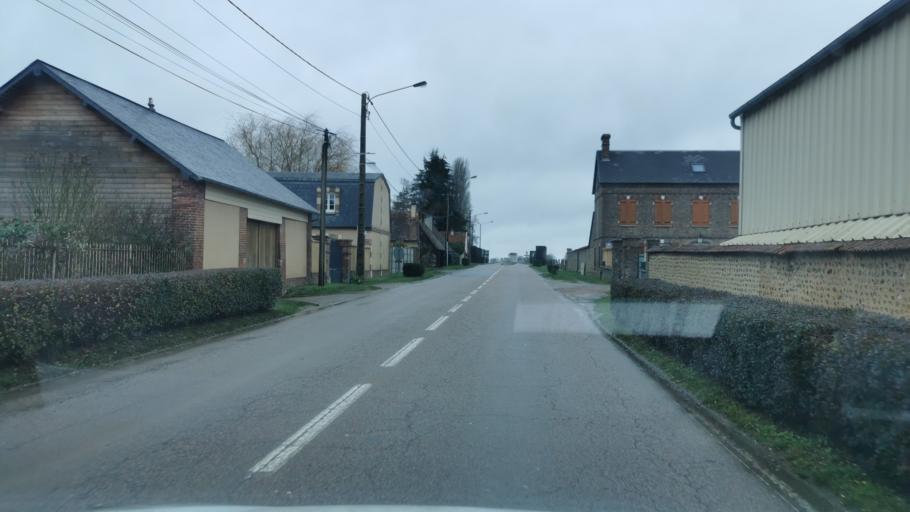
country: FR
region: Haute-Normandie
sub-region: Departement de l'Eure
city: Normanville
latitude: 49.0844
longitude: 1.1805
